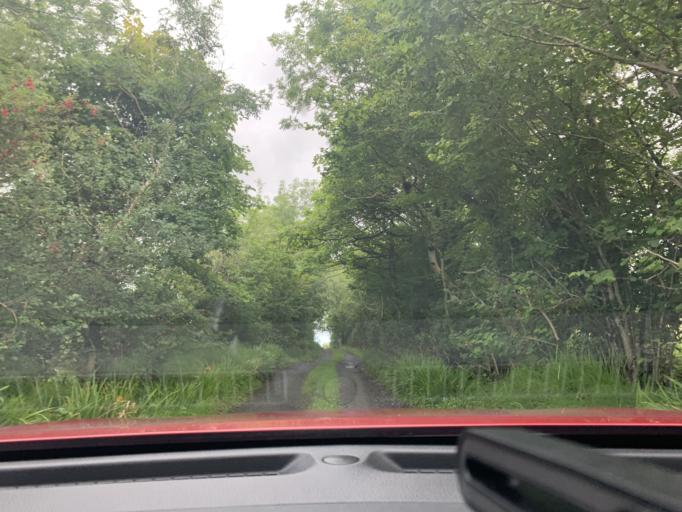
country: IE
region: Connaught
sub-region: Sligo
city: Sligo
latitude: 54.3284
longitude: -8.4153
